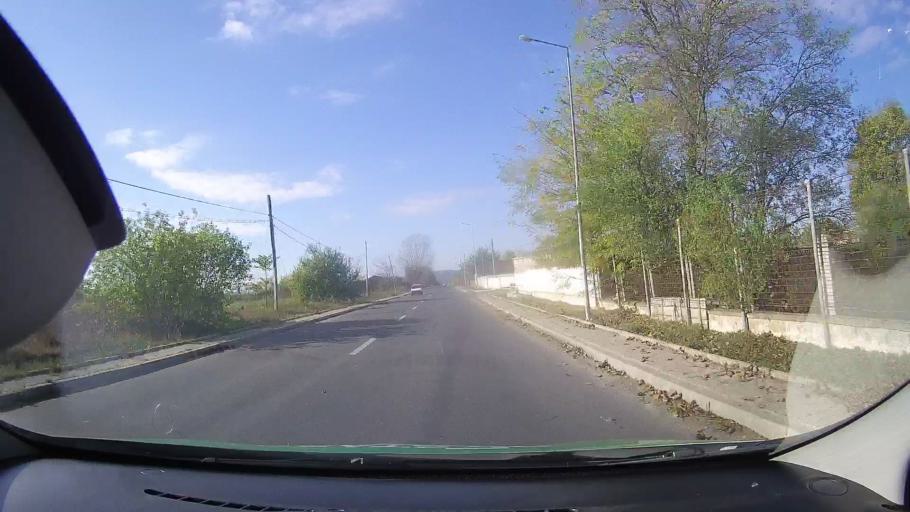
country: RO
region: Tulcea
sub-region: Comuna Valea Nucarilor
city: Valea Nucarilor
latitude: 45.0412
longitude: 28.9282
